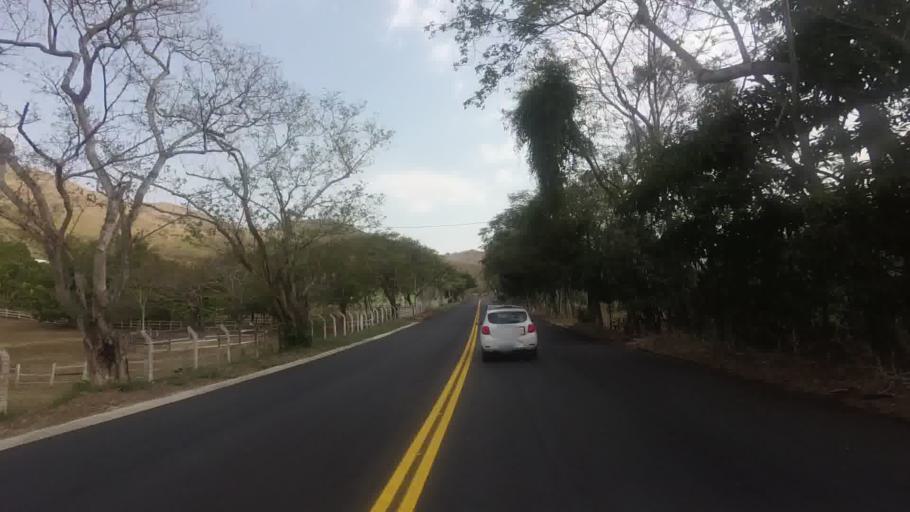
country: BR
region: Rio de Janeiro
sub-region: Bom Jesus Do Itabapoana
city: Bom Jesus do Itabapoana
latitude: -21.2177
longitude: -41.7381
